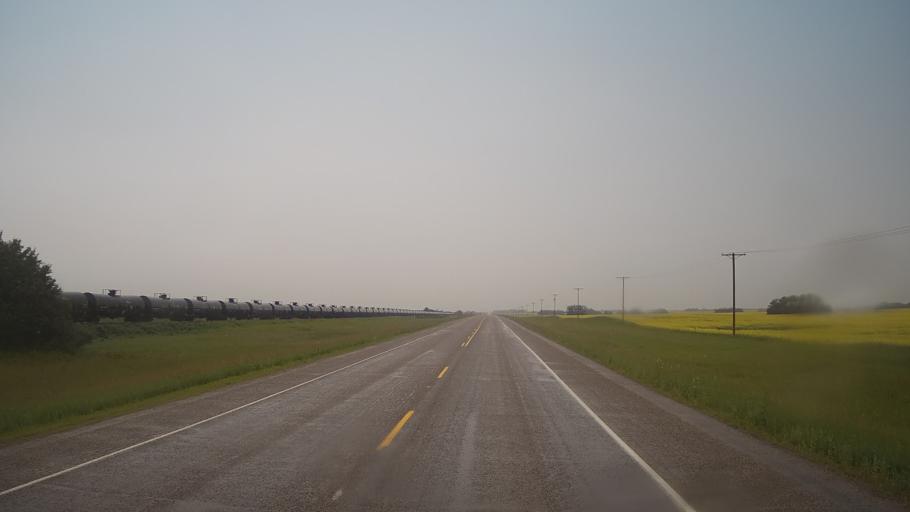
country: CA
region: Saskatchewan
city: Biggar
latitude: 52.1601
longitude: -108.2759
